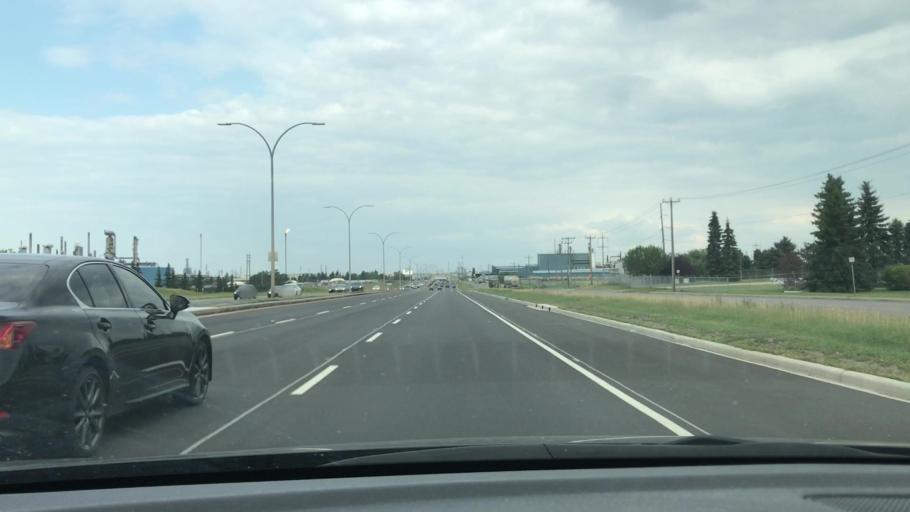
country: CA
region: Alberta
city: Edmonton
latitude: 53.5410
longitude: -113.4088
